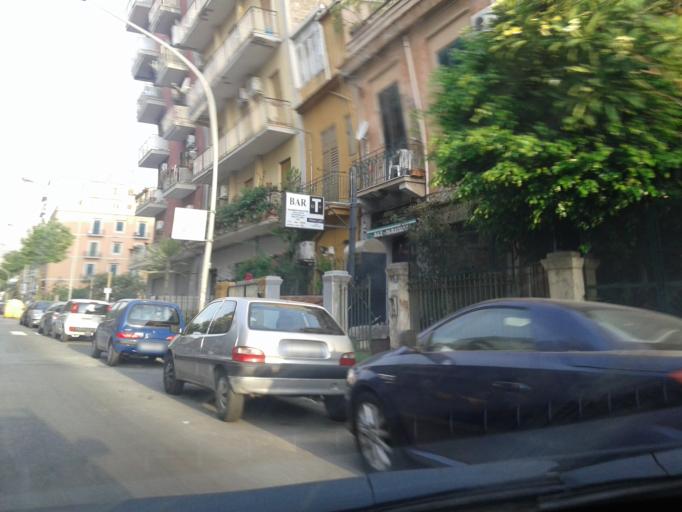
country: IT
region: Sicily
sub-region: Palermo
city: Palermo
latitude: 38.1104
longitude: 13.3359
